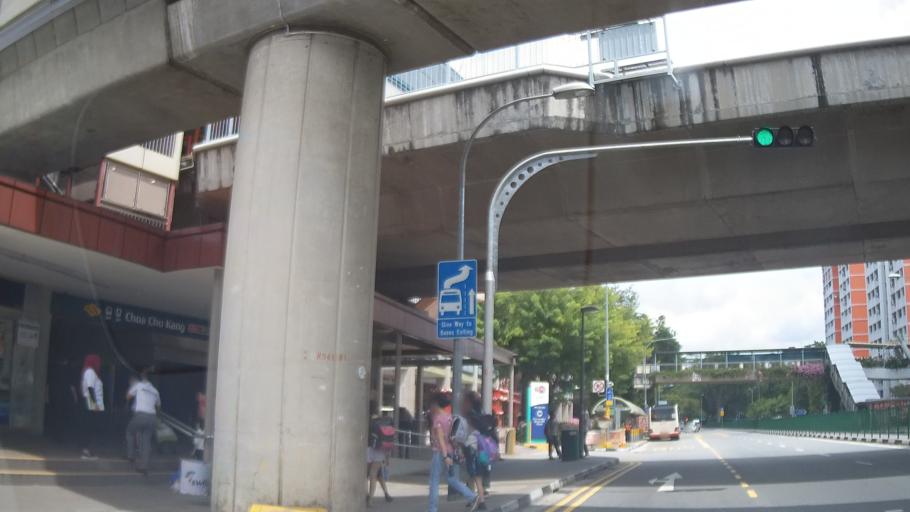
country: MY
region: Johor
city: Johor Bahru
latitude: 1.3843
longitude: 103.7442
